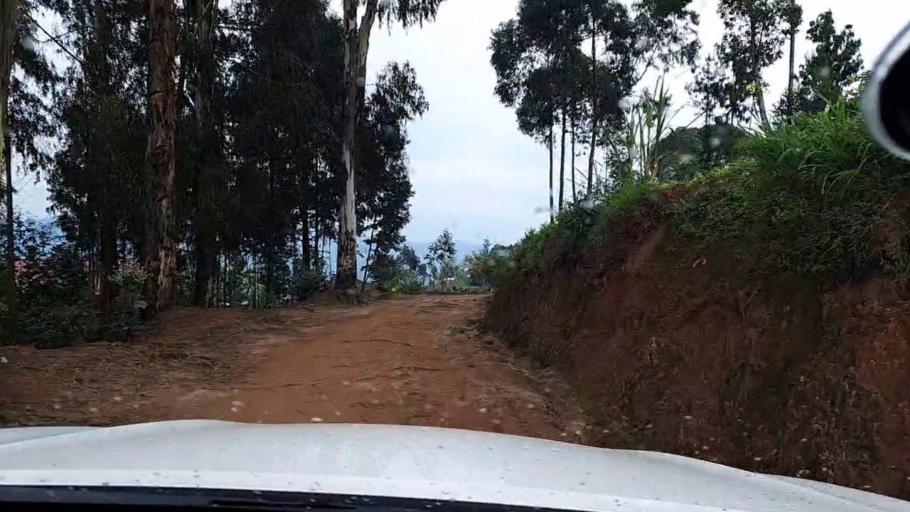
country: RW
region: Southern Province
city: Nzega
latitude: -2.3815
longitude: 29.2409
